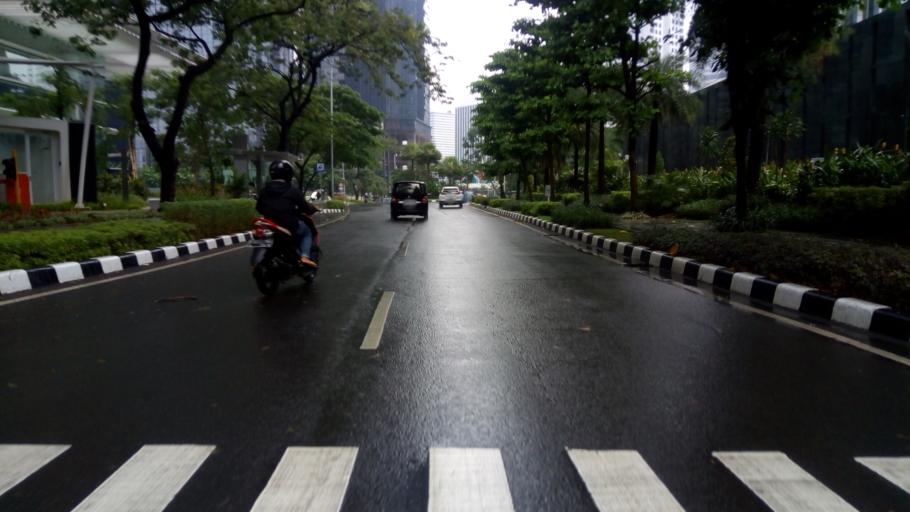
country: ID
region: Jakarta Raya
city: Jakarta
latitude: -6.2272
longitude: 106.8088
